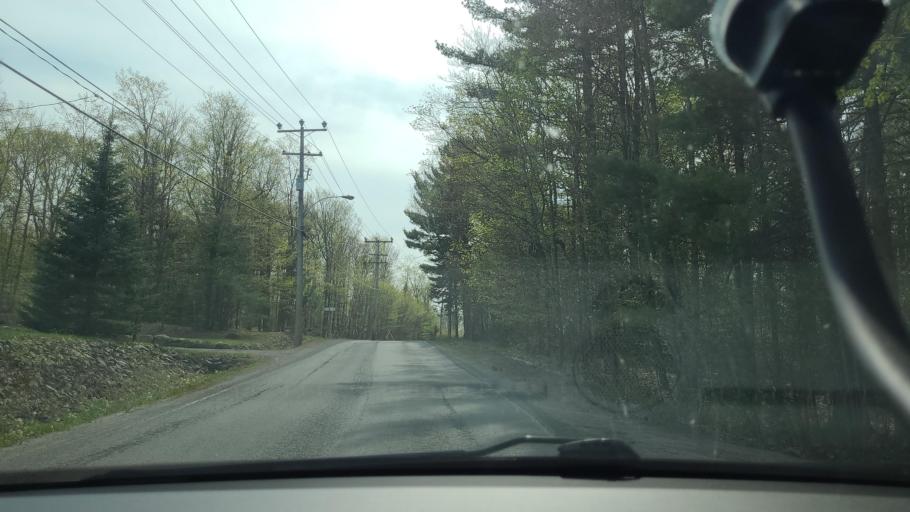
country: CA
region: Quebec
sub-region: Laurentides
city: Prevost
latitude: 45.8923
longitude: -74.0443
